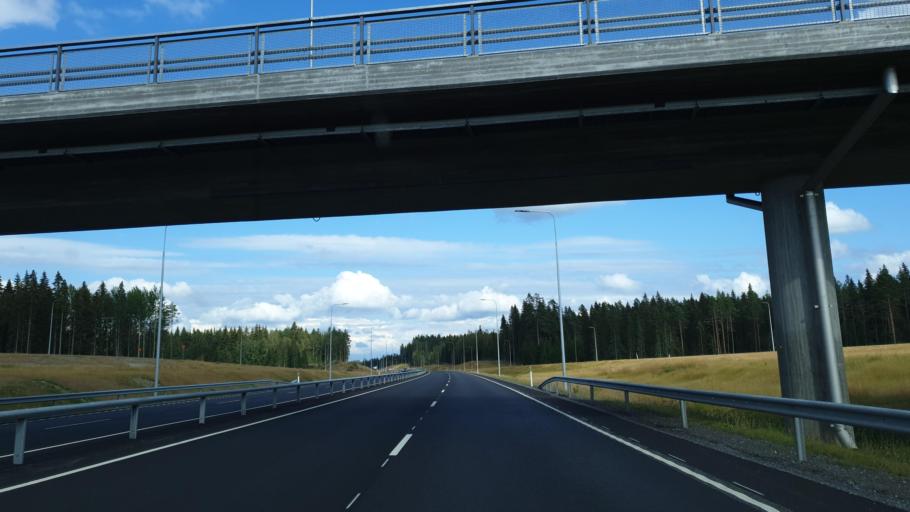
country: FI
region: Southern Savonia
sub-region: Mikkeli
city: Mikkeli
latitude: 61.7353
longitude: 27.4170
